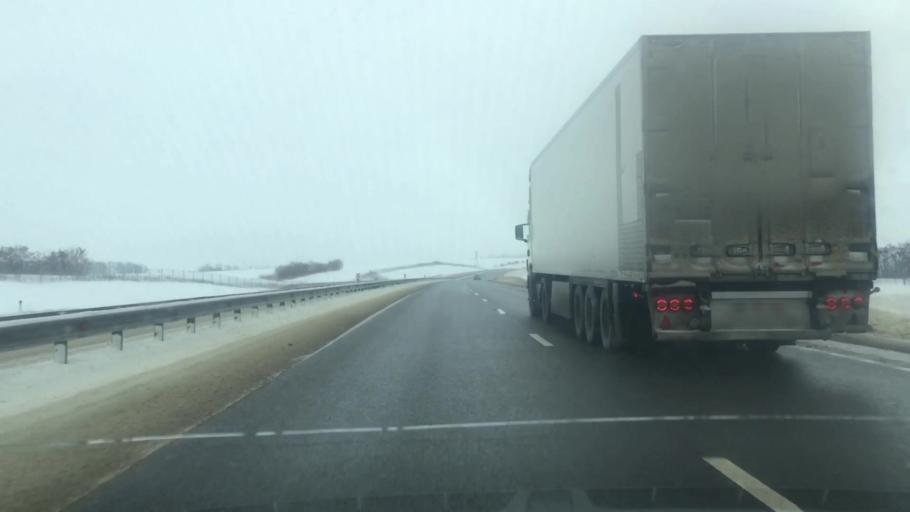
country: RU
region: Tula
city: Yefremov
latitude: 53.1529
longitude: 38.2503
